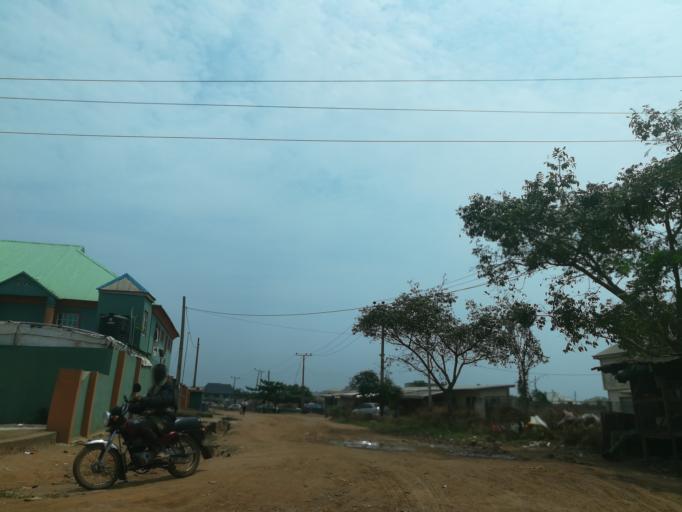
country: NG
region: Lagos
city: Ikorodu
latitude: 6.6035
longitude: 3.6070
